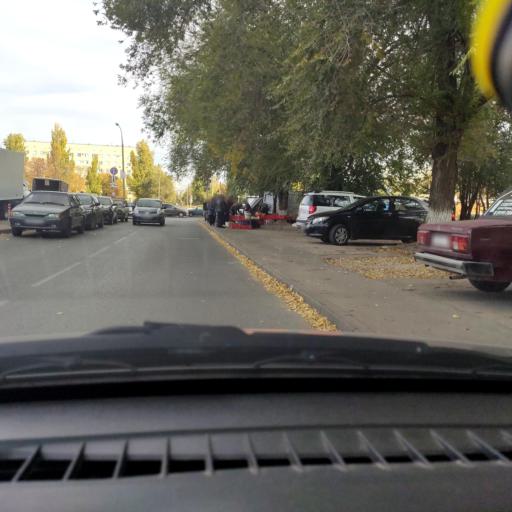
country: RU
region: Samara
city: Tol'yatti
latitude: 53.5293
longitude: 49.2661
